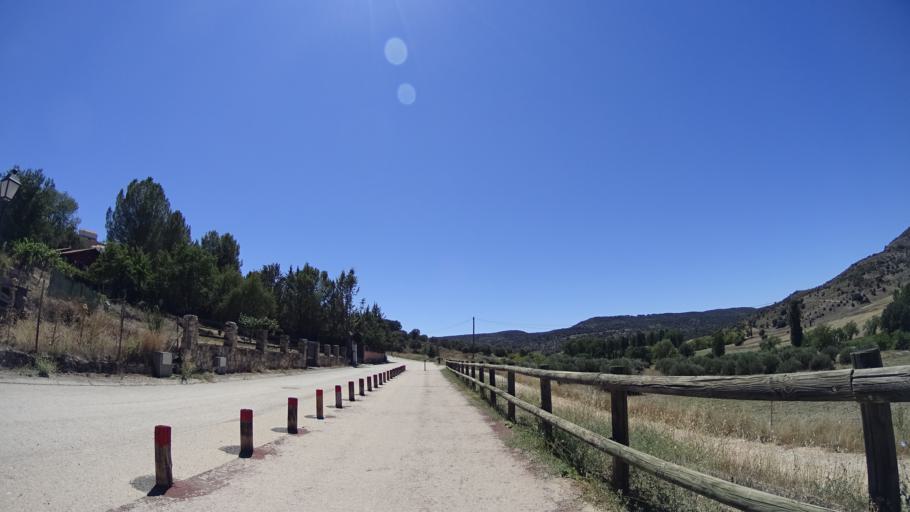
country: ES
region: Madrid
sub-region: Provincia de Madrid
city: Ambite
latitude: 40.3213
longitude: -3.1826
